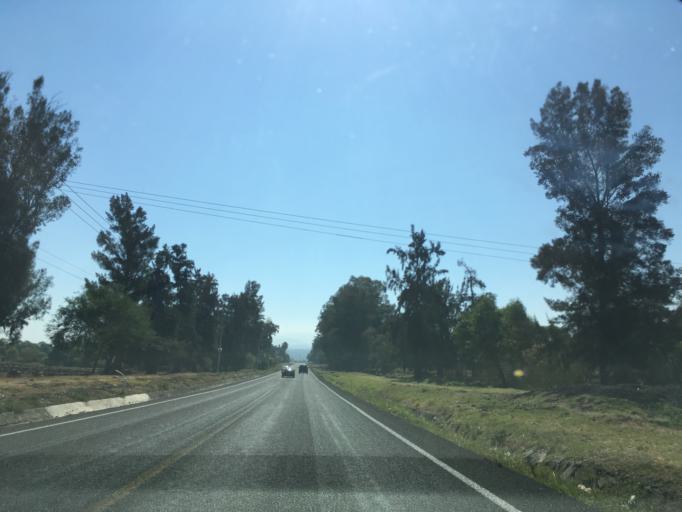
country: MX
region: Michoacan
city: Indaparapeo
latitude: 19.7939
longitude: -100.9505
